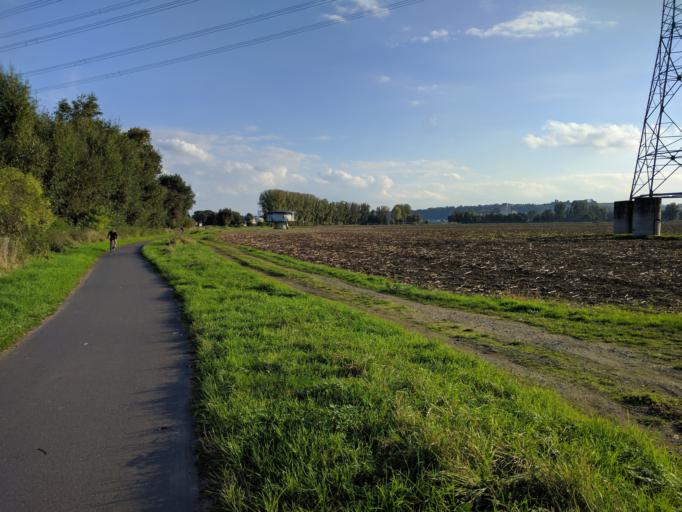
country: DE
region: Saxony
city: Heidenau
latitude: 50.9874
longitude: 13.8801
